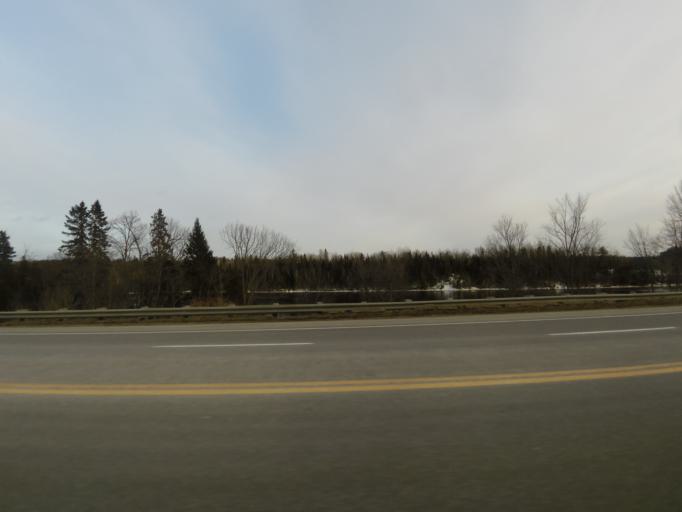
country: CA
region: Quebec
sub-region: Outaouais
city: Wakefield
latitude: 45.7026
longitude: -75.9277
